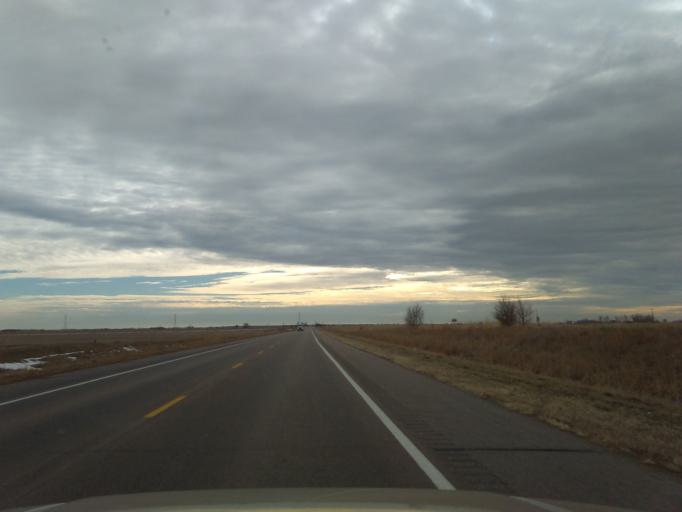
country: US
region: Nebraska
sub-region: Kearney County
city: Minden
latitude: 40.5667
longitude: -98.9519
